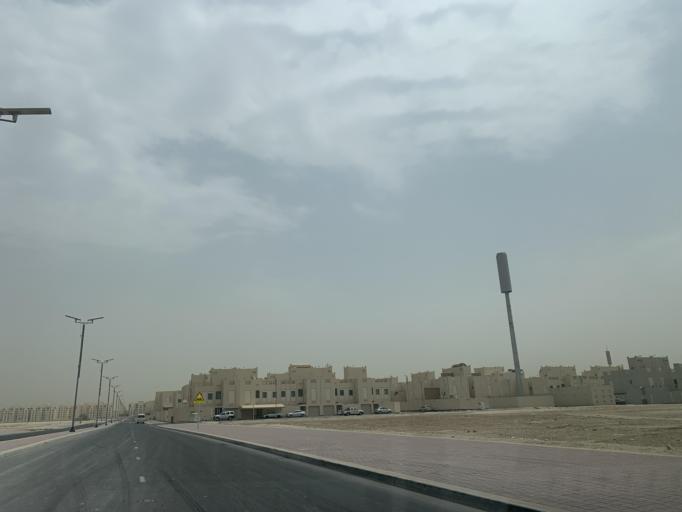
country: BH
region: Northern
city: Madinat `Isa
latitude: 26.1739
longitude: 50.5107
